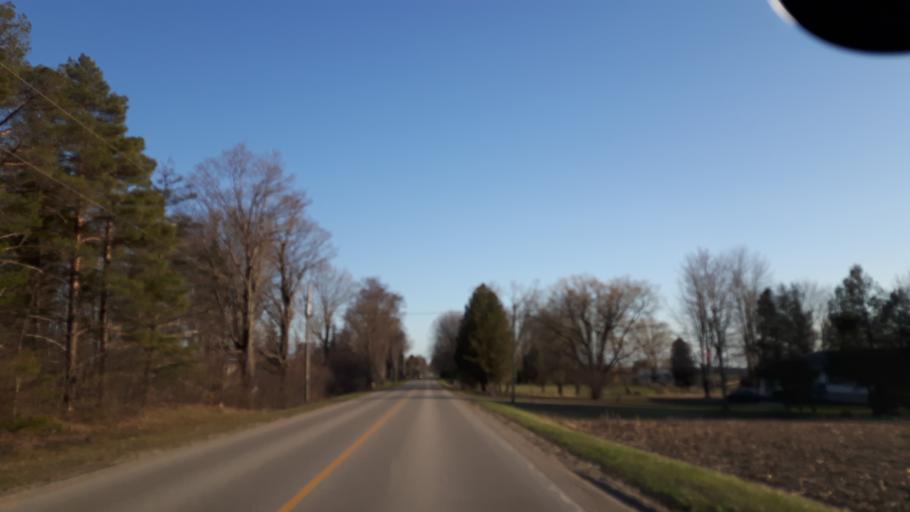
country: CA
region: Ontario
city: Goderich
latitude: 43.7138
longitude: -81.6852
